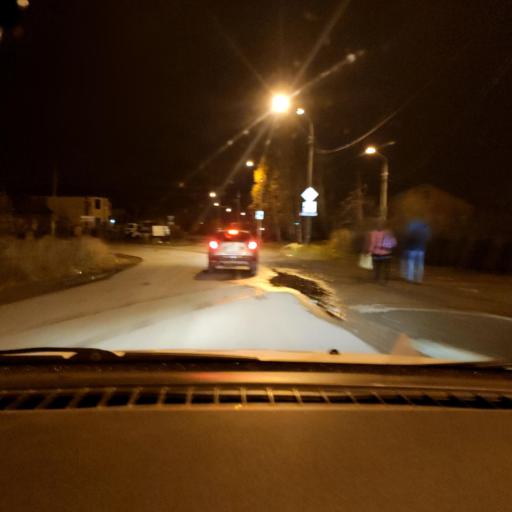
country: RU
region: Perm
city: Perm
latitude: 58.0417
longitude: 56.3552
